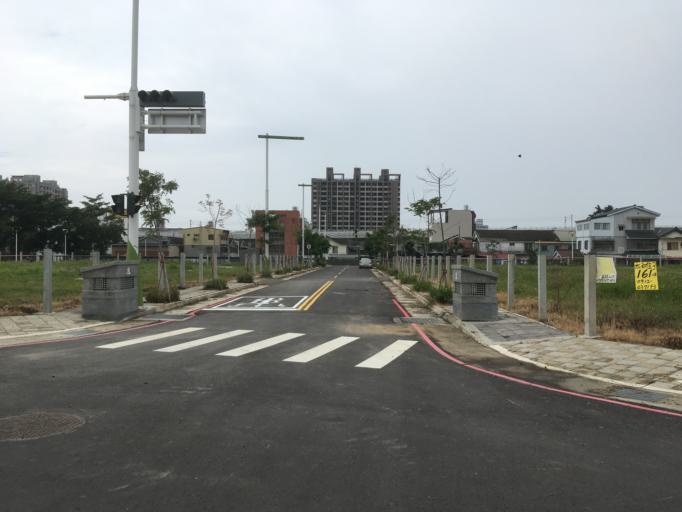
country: TW
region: Taiwan
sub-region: Taichung City
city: Taichung
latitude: 24.1926
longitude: 120.7059
